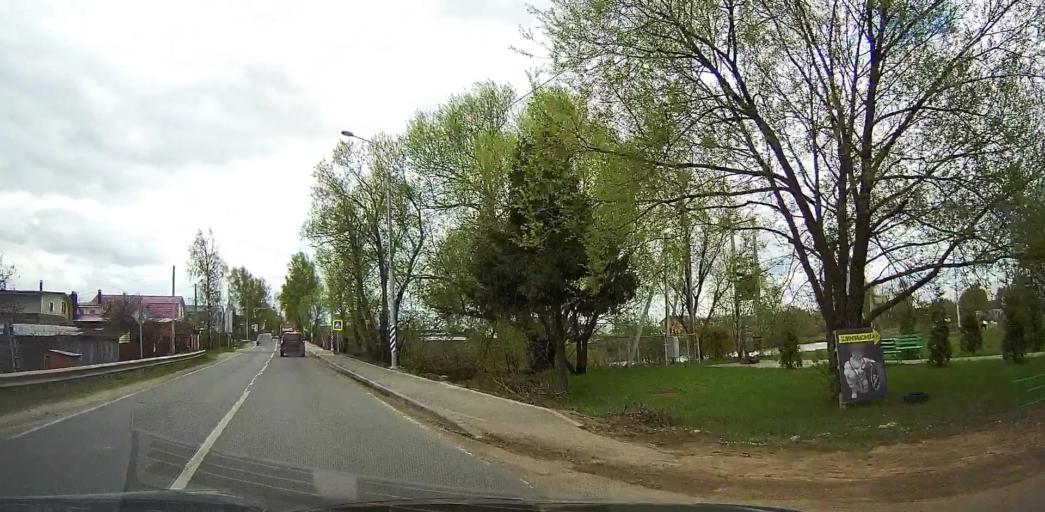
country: RU
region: Moskovskaya
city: Beloozerskiy
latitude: 55.4723
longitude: 38.4131
